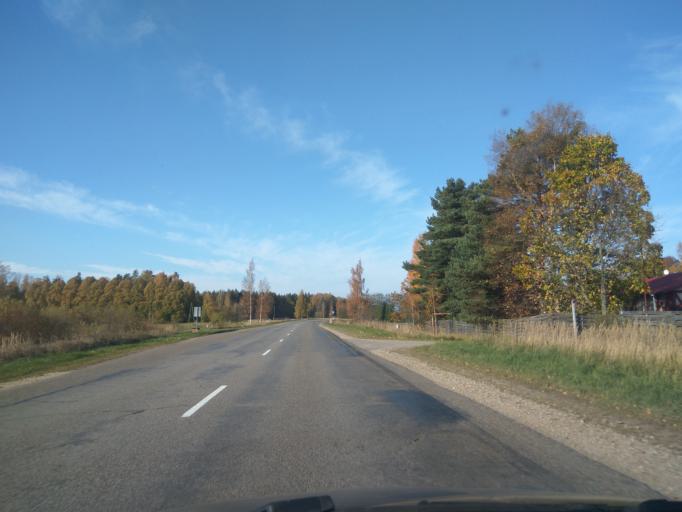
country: LV
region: Ventspils
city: Ventspils
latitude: 57.2837
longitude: 21.5717
